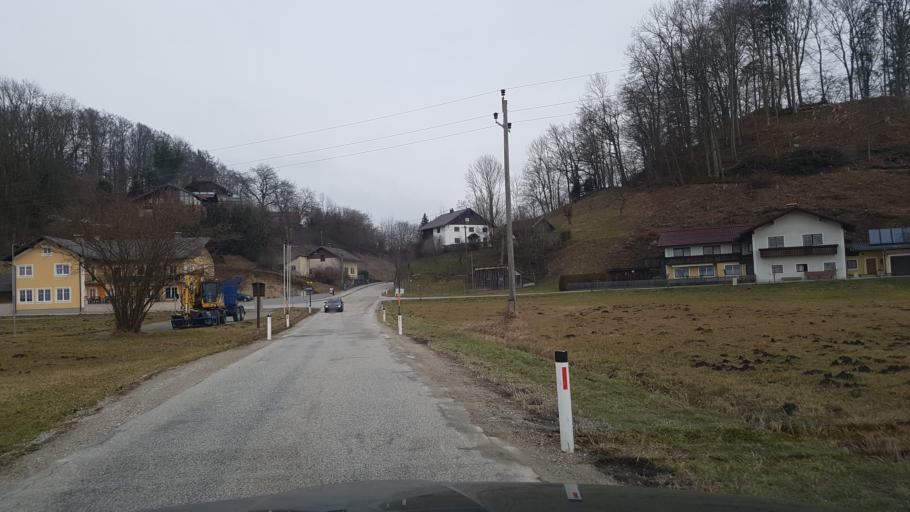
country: AT
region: Salzburg
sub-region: Politischer Bezirk Salzburg-Umgebung
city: Dorfbeuern
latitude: 48.0635
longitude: 12.9617
